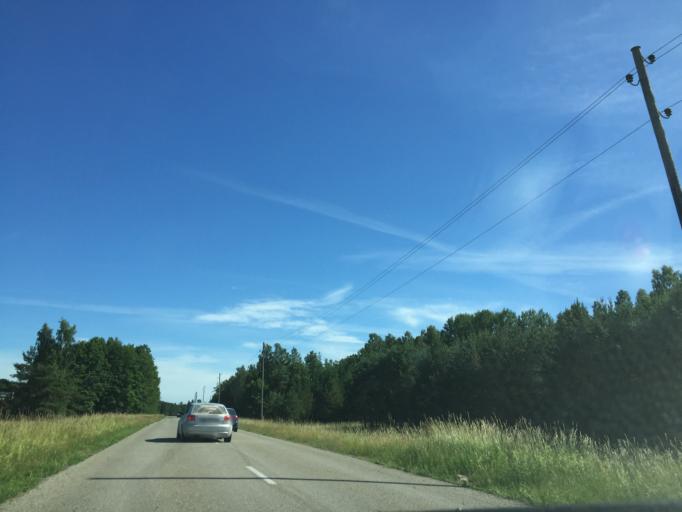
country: LV
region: Rojas
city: Roja
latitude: 57.4694
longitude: 22.8698
